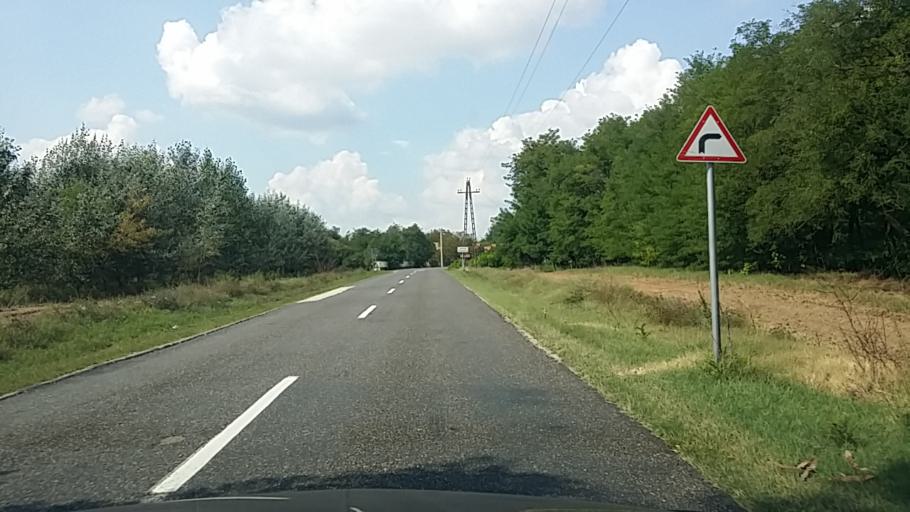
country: HU
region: Bacs-Kiskun
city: Lakitelek
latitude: 46.8646
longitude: 19.9643
